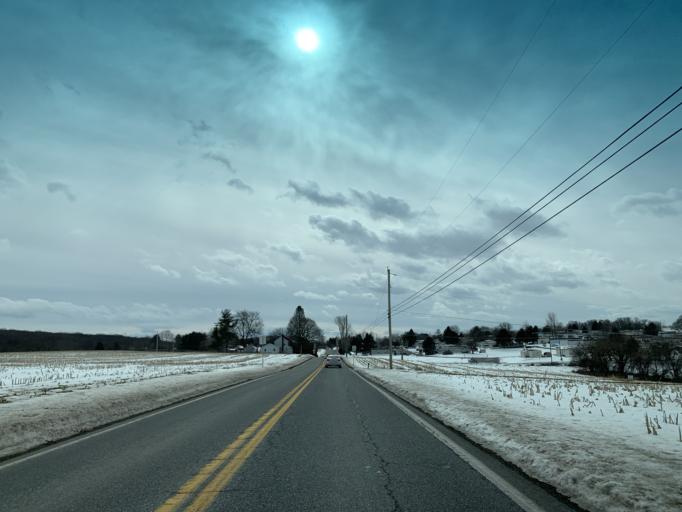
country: US
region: Pennsylvania
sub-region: York County
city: Shrewsbury
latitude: 39.7971
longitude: -76.6331
